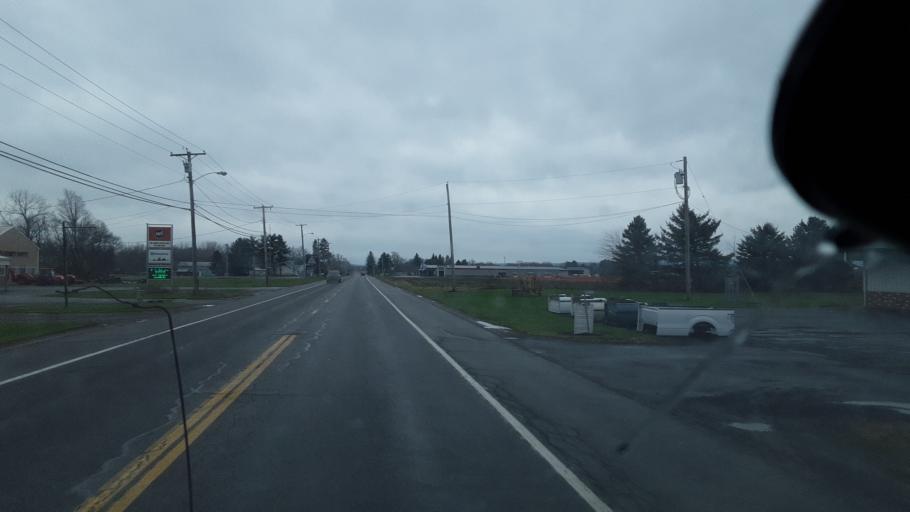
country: US
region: New York
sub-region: Cattaraugus County
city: Yorkshire
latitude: 42.5504
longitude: -78.4781
